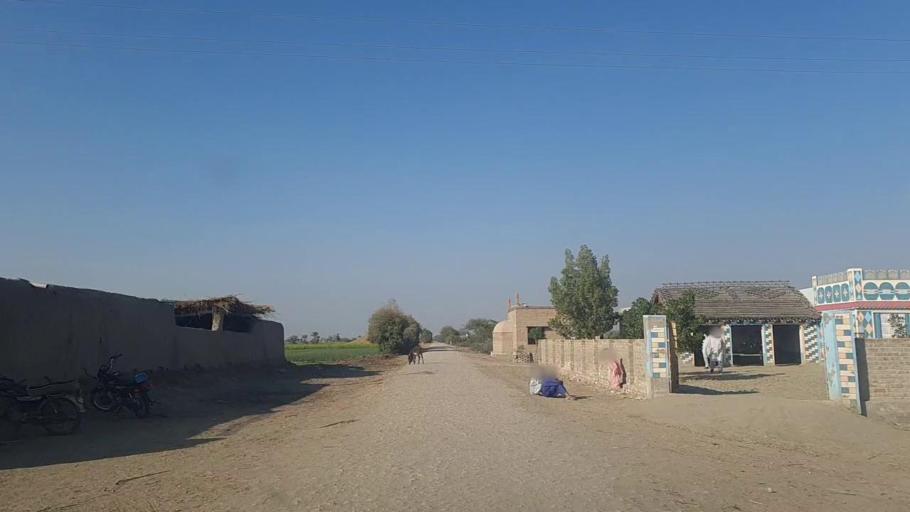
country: PK
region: Sindh
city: Jam Sahib
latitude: 26.3202
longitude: 68.7147
